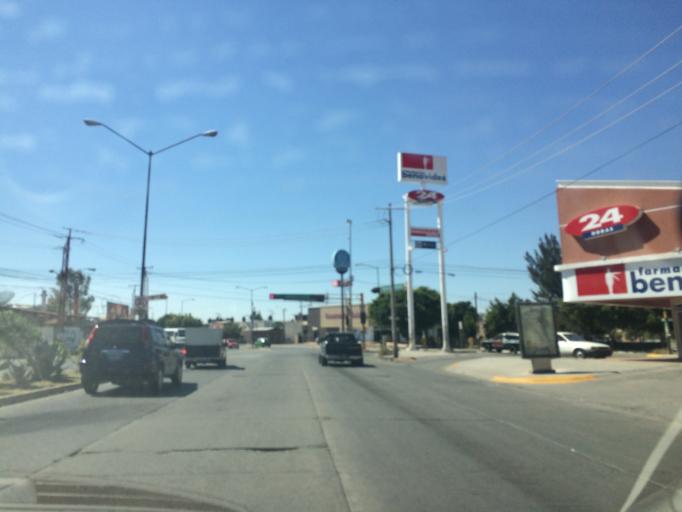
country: MX
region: Guanajuato
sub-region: Leon
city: San Jose de Duran (Los Troncoso)
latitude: 21.0808
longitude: -101.6513
